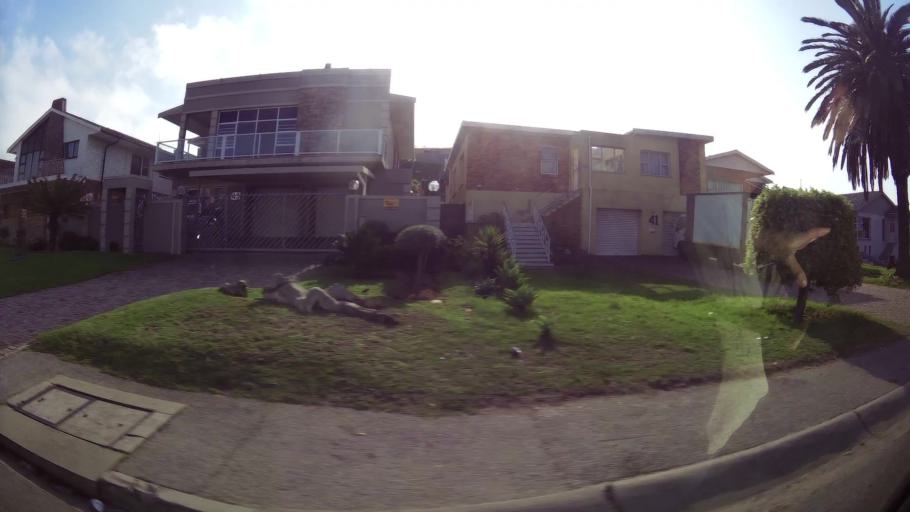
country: ZA
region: Eastern Cape
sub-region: Nelson Mandela Bay Metropolitan Municipality
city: Port Elizabeth
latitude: -33.9265
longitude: 25.5430
